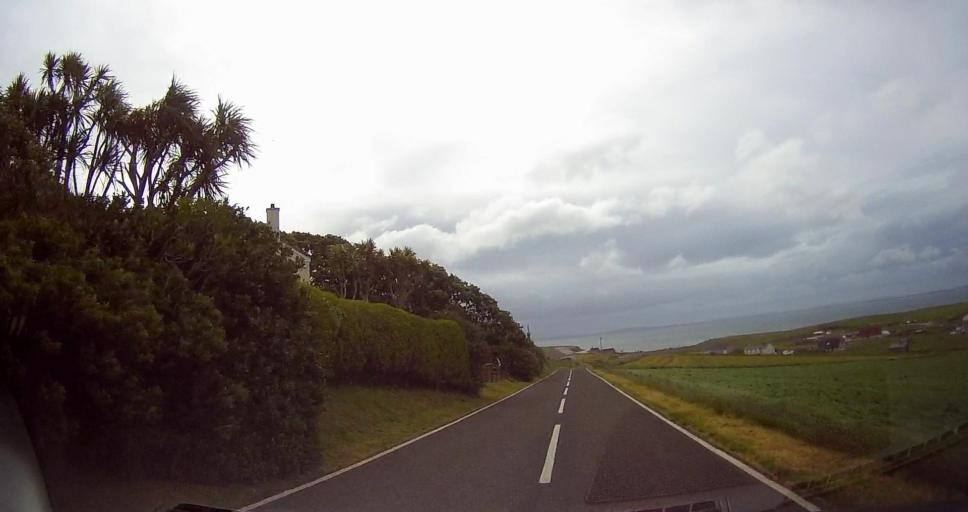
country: GB
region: Scotland
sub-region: Orkney Islands
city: Stromness
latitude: 58.9210
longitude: -3.1867
